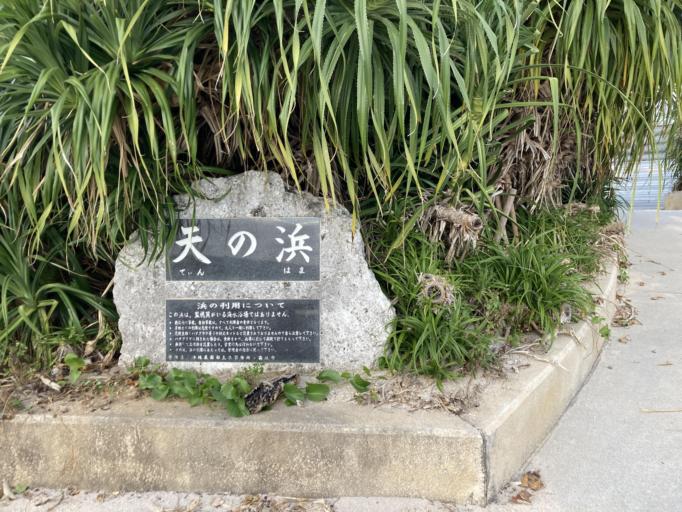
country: JP
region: Okinawa
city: Ginowan
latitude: 26.1825
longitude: 127.7785
